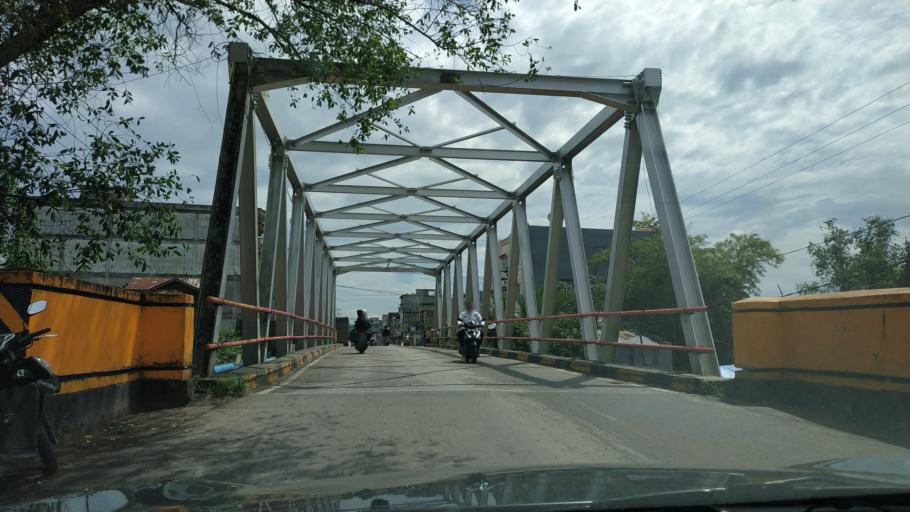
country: ID
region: Riau
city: Tembilahan
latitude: -0.3266
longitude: 103.1441
